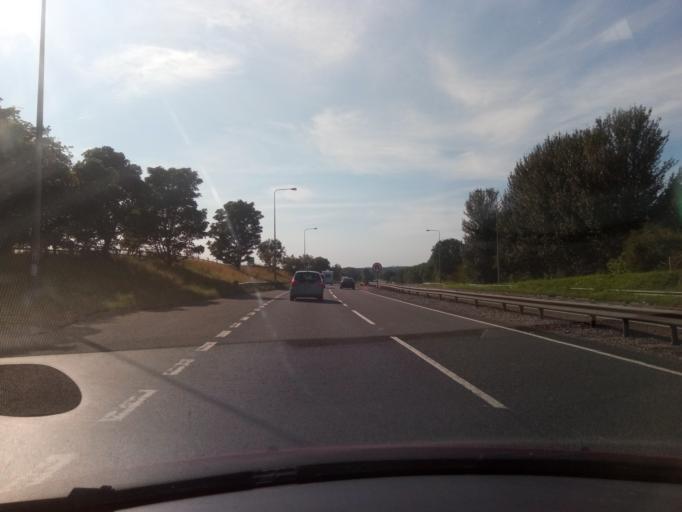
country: GB
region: England
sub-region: Hartlepool
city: Elwick
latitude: 54.6674
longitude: -1.3001
